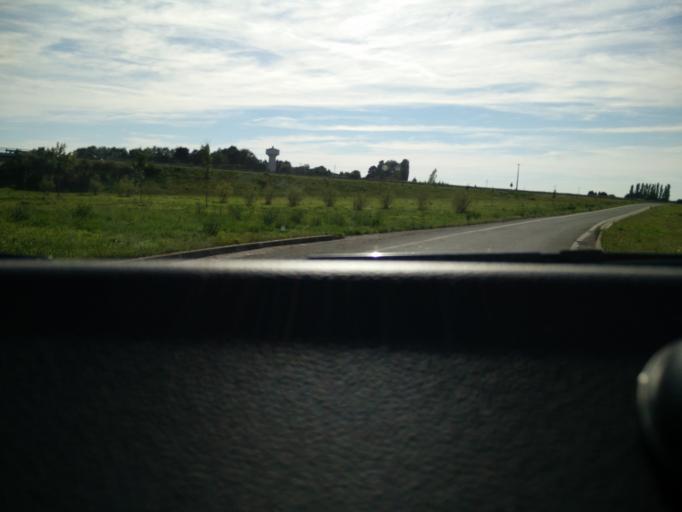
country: FR
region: Nord-Pas-de-Calais
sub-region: Departement du Nord
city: Louvroil
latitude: 50.2488
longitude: 3.9541
